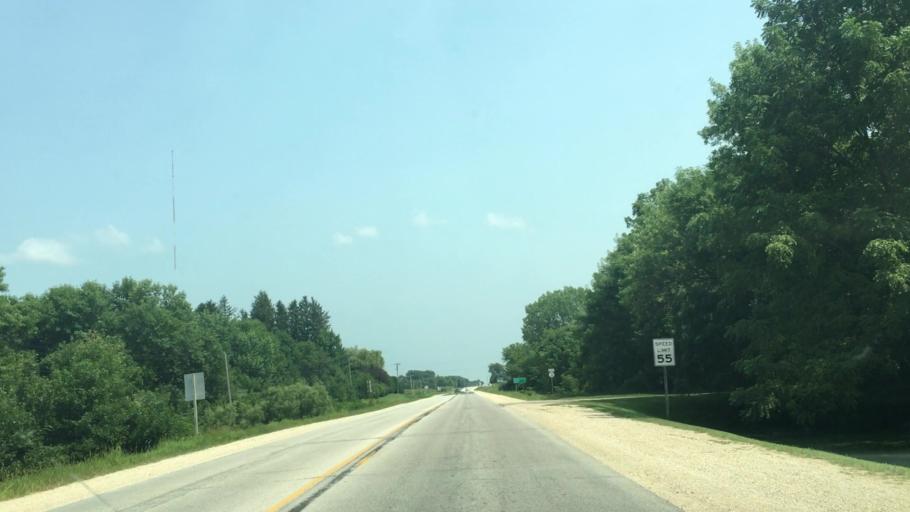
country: US
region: Iowa
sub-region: Fayette County
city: Oelwein
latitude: 42.6791
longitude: -91.8930
